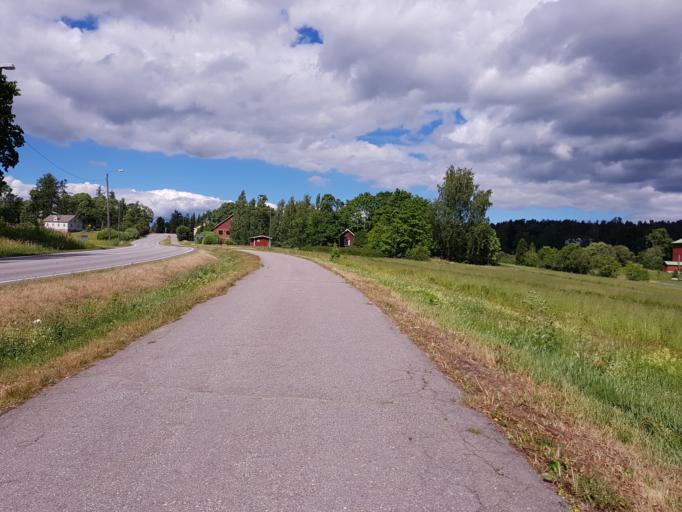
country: FI
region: Uusimaa
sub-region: Helsinki
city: Nurmijaervi
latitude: 60.3450
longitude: 24.8667
